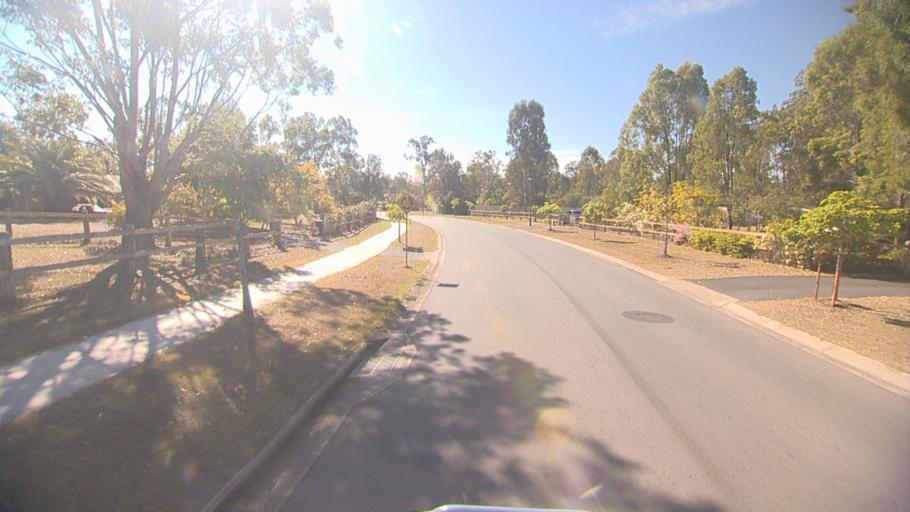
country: AU
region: Queensland
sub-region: Logan
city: North Maclean
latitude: -27.8103
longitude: 152.9627
